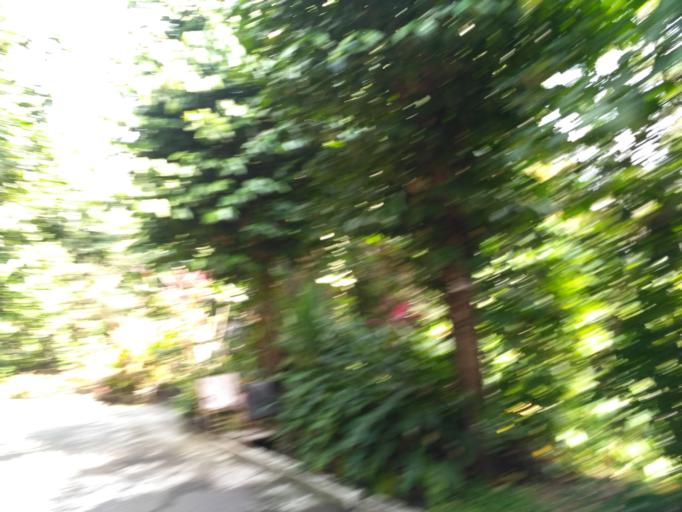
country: ID
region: Daerah Istimewa Yogyakarta
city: Depok
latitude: -7.7403
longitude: 110.4100
